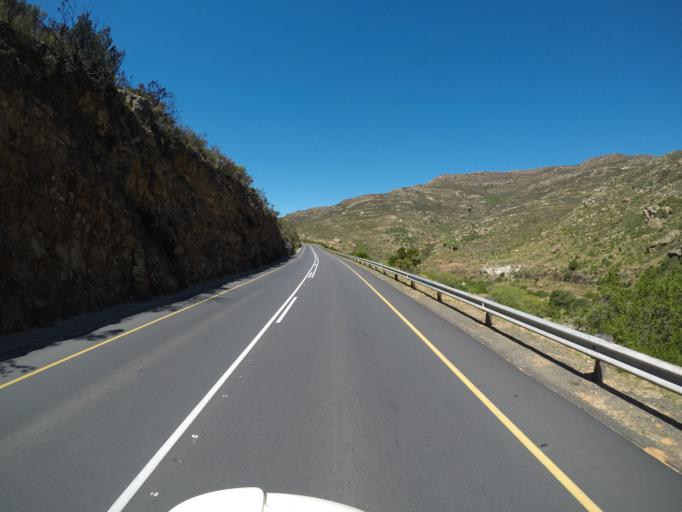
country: ZA
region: Western Cape
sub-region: Cape Winelands District Municipality
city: Ceres
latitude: -33.3170
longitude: 19.0793
